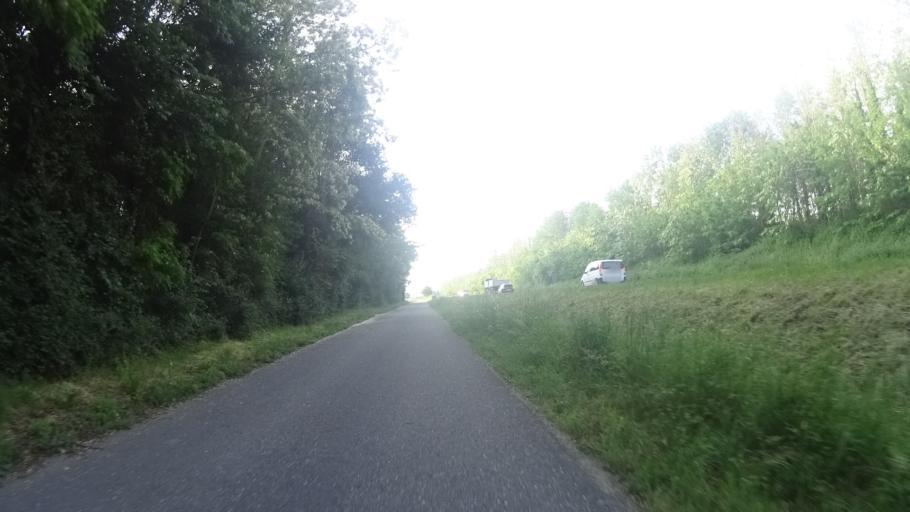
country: DE
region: Baden-Wuerttemberg
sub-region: Freiburg Region
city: Merdingen
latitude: 47.9887
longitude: 7.6375
